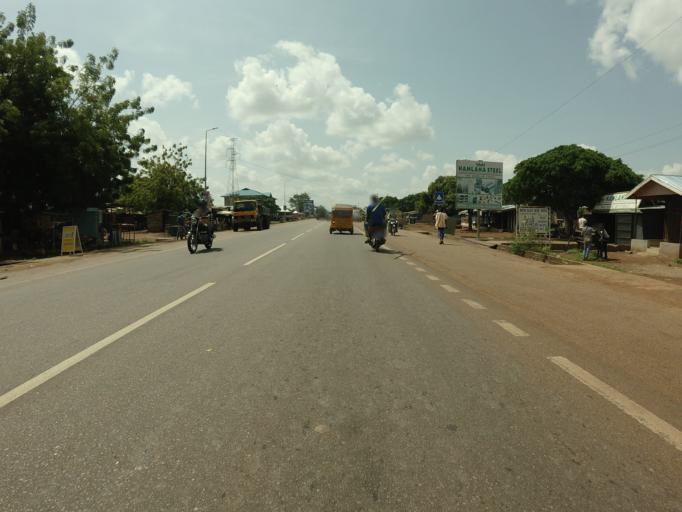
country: GH
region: Northern
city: Tamale
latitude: 9.4478
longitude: -0.8446
